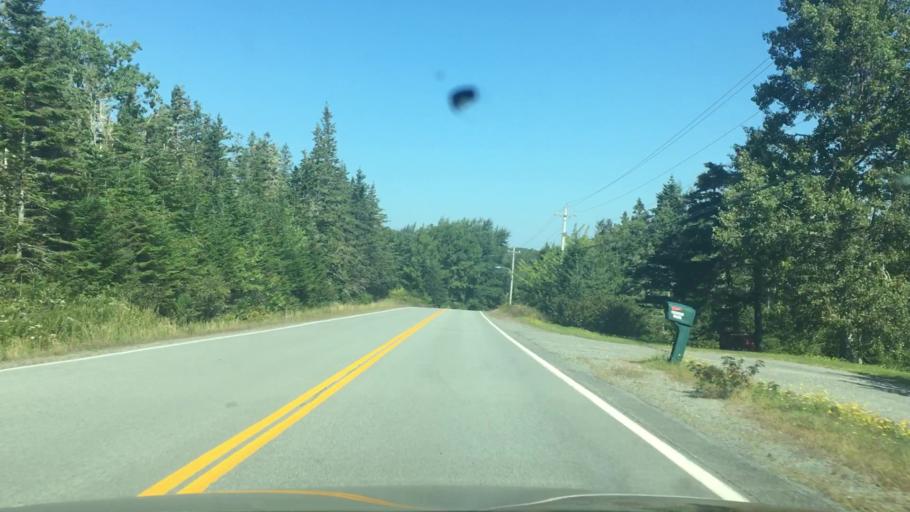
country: CA
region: Nova Scotia
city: New Glasgow
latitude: 44.8195
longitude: -62.6341
